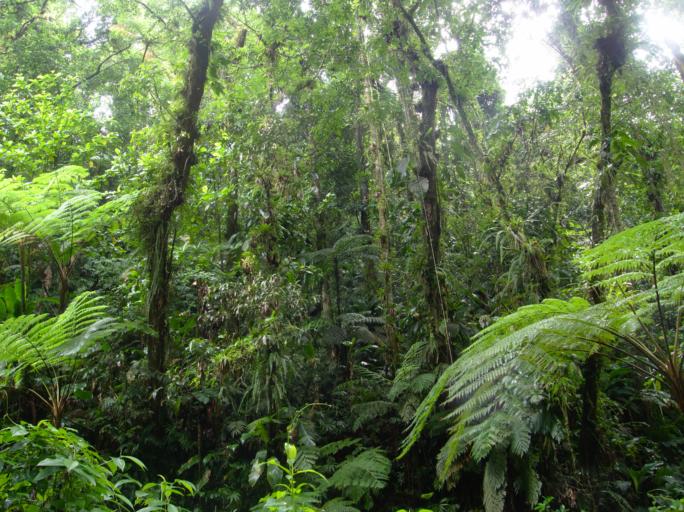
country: MQ
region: Martinique
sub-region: Martinique
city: Saint-Joseph
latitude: 14.6763
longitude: -61.0951
